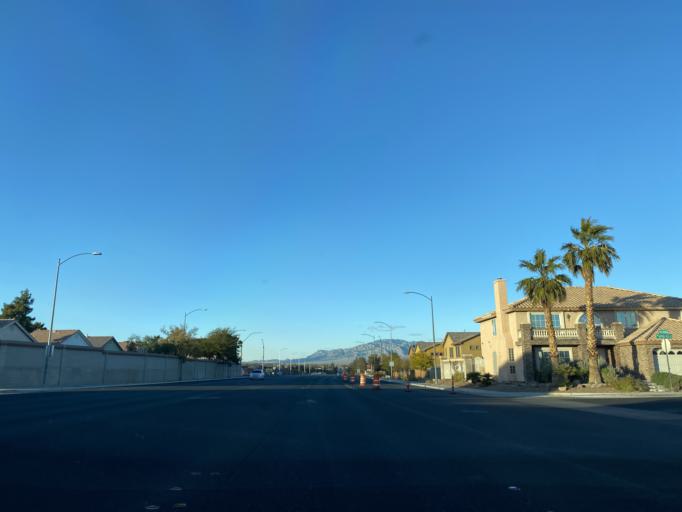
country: US
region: Nevada
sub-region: Clark County
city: Summerlin South
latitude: 36.2321
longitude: -115.2976
